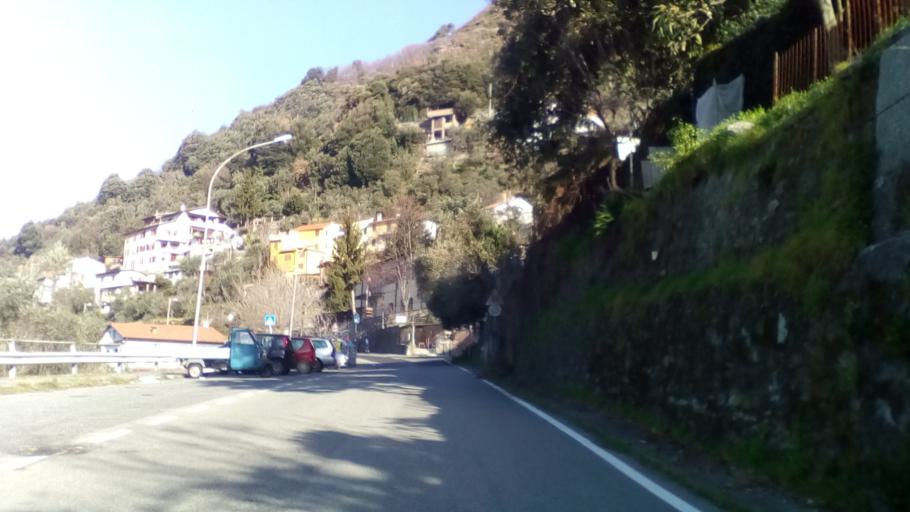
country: IT
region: Tuscany
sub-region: Provincia di Massa-Carrara
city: Montignoso
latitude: 44.0581
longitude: 10.1812
